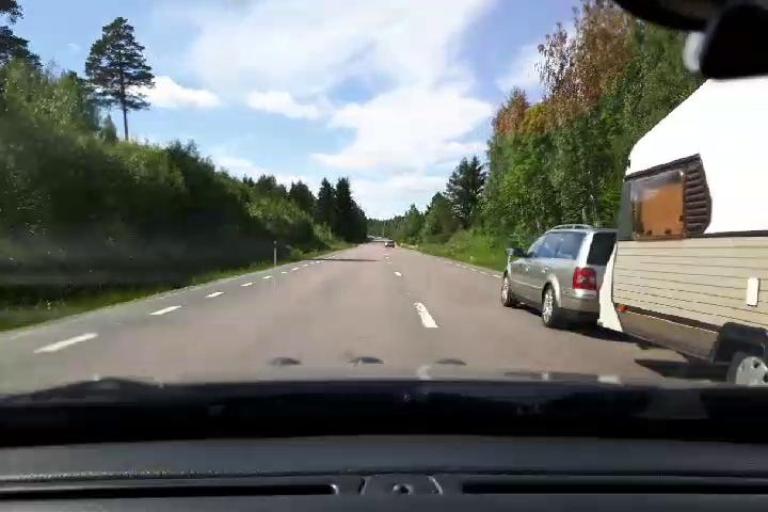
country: SE
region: Gaevleborg
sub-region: Bollnas Kommun
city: Kilafors
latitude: 61.2935
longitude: 16.4969
